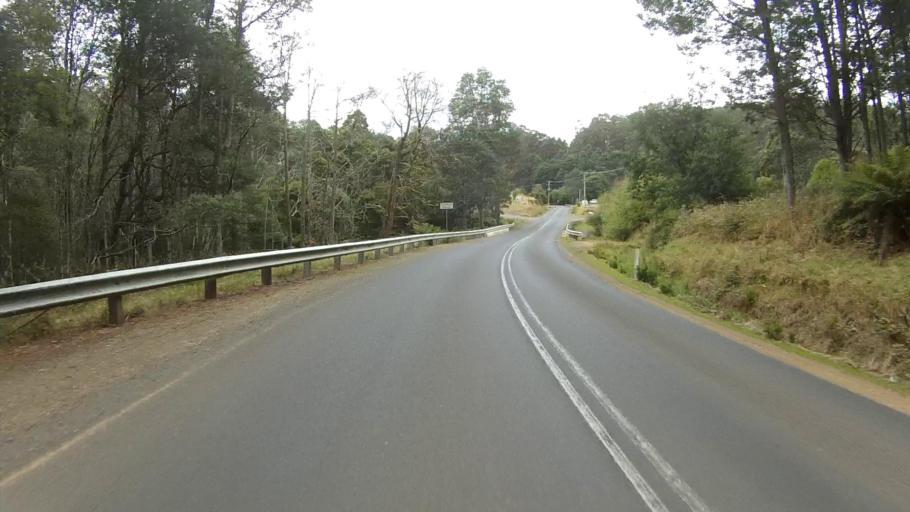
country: AU
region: Tasmania
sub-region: Huon Valley
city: Cygnet
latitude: -43.1436
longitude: 147.1535
